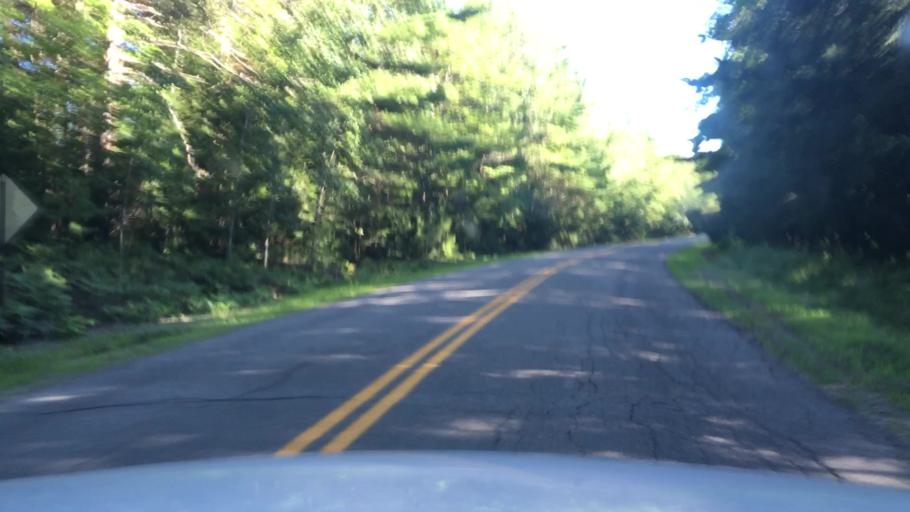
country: US
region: Maine
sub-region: Penobscot County
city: Enfield
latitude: 45.2229
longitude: -68.5801
